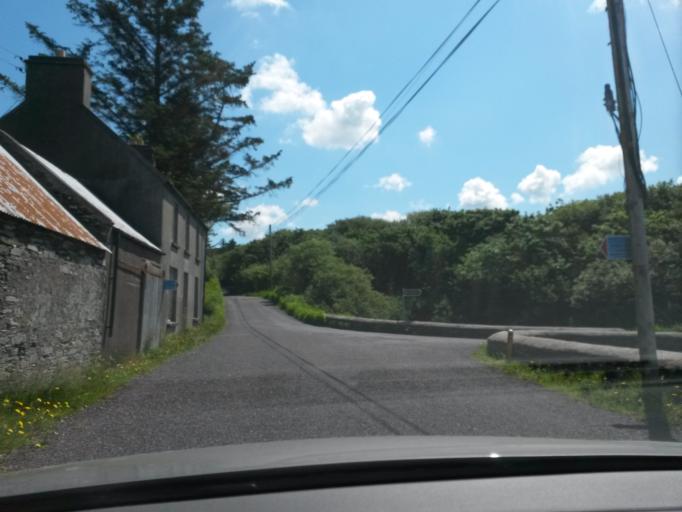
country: IE
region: Munster
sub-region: Ciarrai
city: Cahersiveen
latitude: 51.7150
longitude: -9.9449
